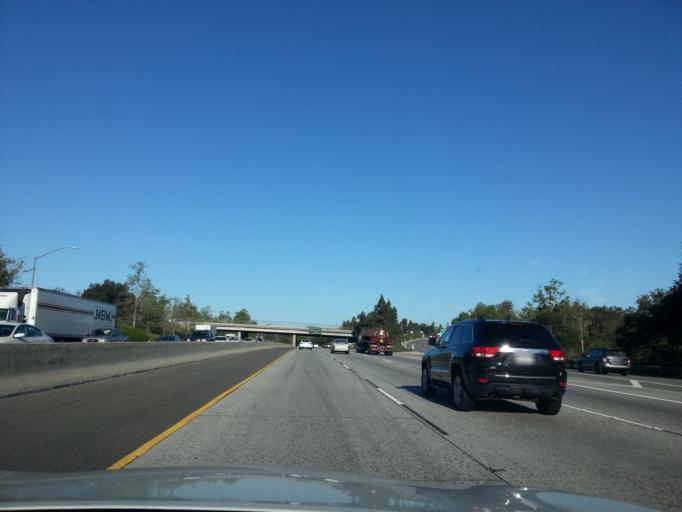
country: US
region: California
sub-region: Ventura County
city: Thousand Oaks
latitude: 34.1823
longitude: -118.8890
